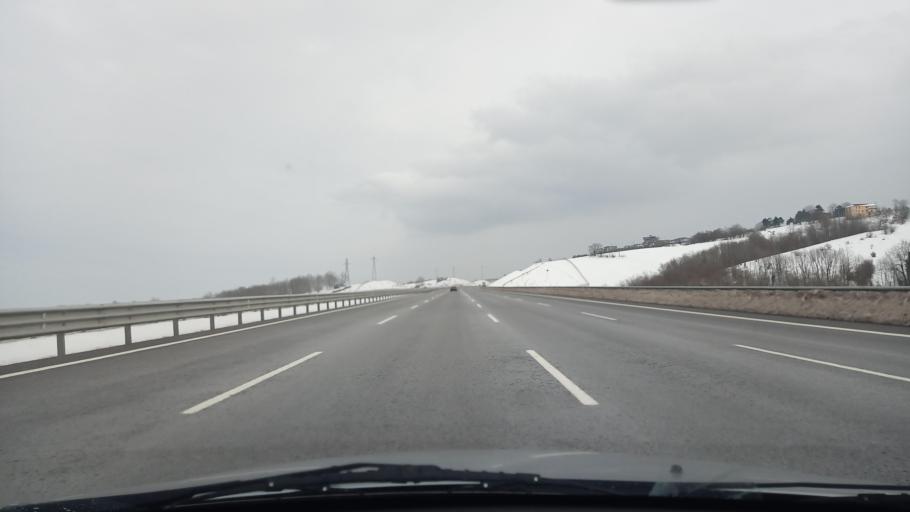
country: TR
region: Kocaeli
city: Derince
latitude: 40.8637
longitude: 29.8321
